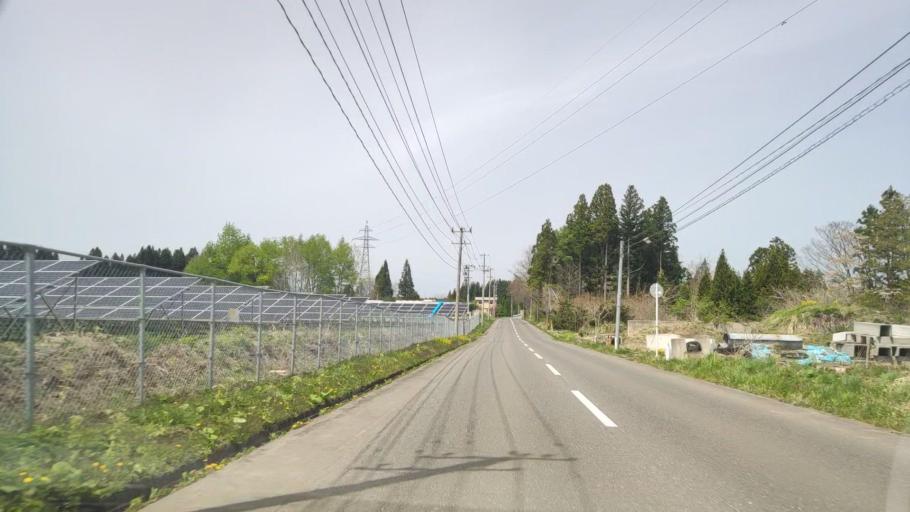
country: JP
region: Aomori
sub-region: Misawa Shi
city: Inuotose
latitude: 40.7209
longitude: 141.1419
